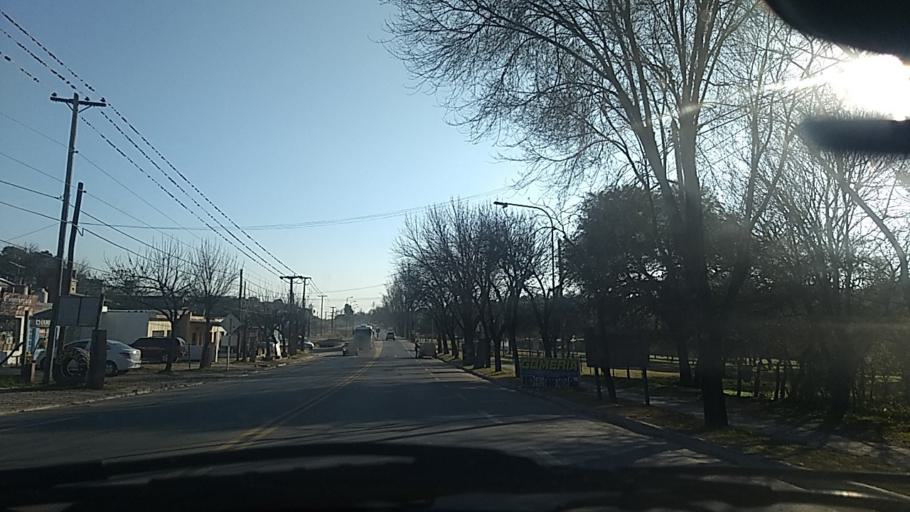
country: AR
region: Cordoba
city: Salsipuedes
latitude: -31.1301
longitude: -64.2951
